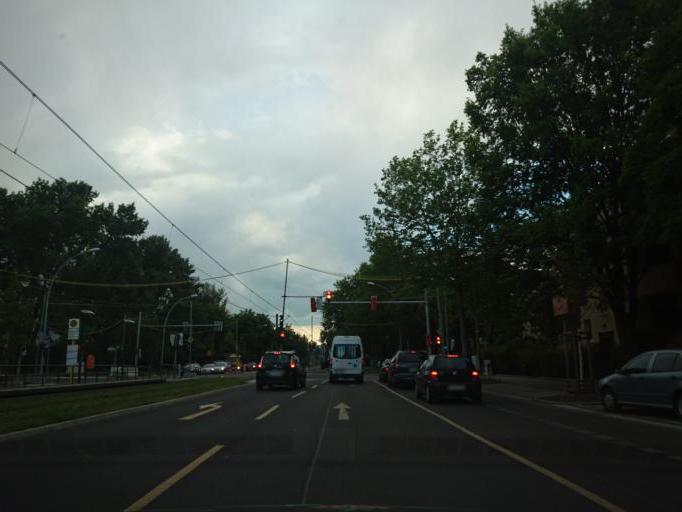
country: DE
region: Berlin
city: Friedrichsfelde
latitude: 52.5006
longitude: 13.5219
